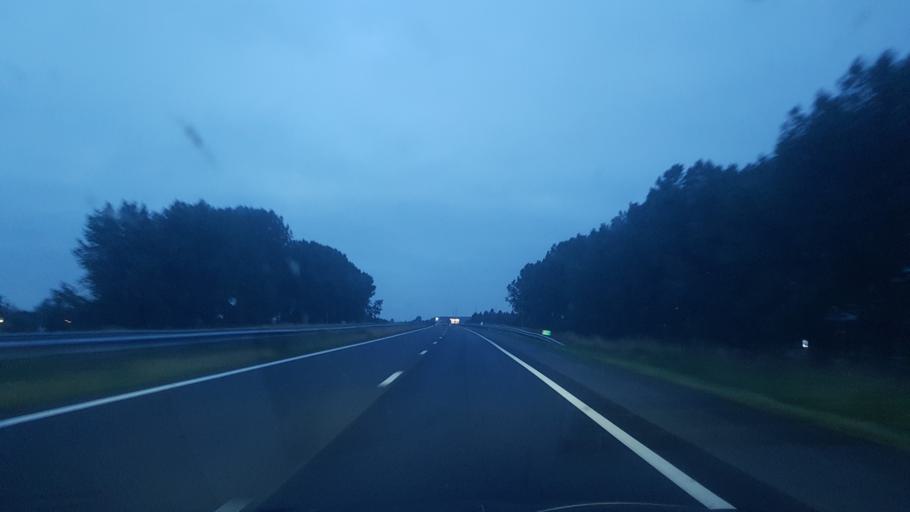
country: NL
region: Friesland
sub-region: Gemeente Boarnsterhim
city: Grou
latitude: 53.0891
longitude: 5.8242
